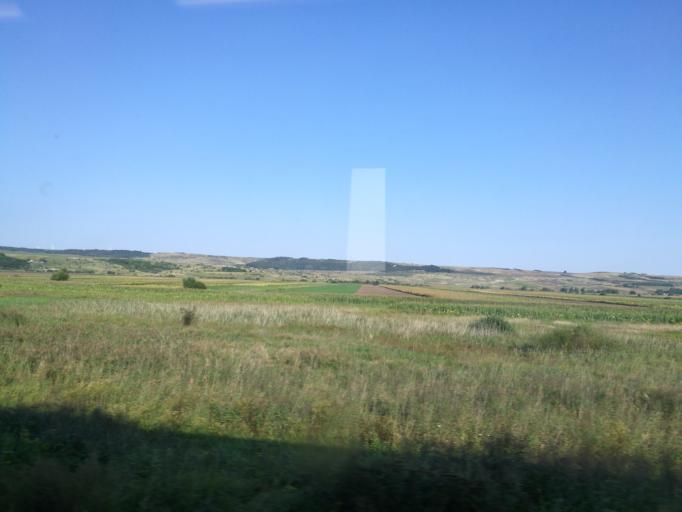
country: RO
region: Vaslui
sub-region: Comuna Albesti
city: Albesti
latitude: 46.4836
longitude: 27.8171
